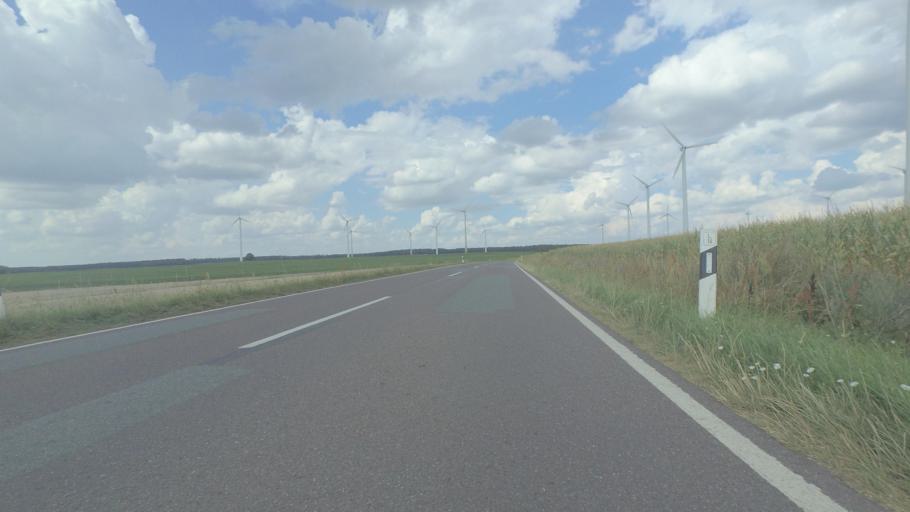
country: DE
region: Brandenburg
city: Wittstock
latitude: 53.2112
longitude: 12.4404
